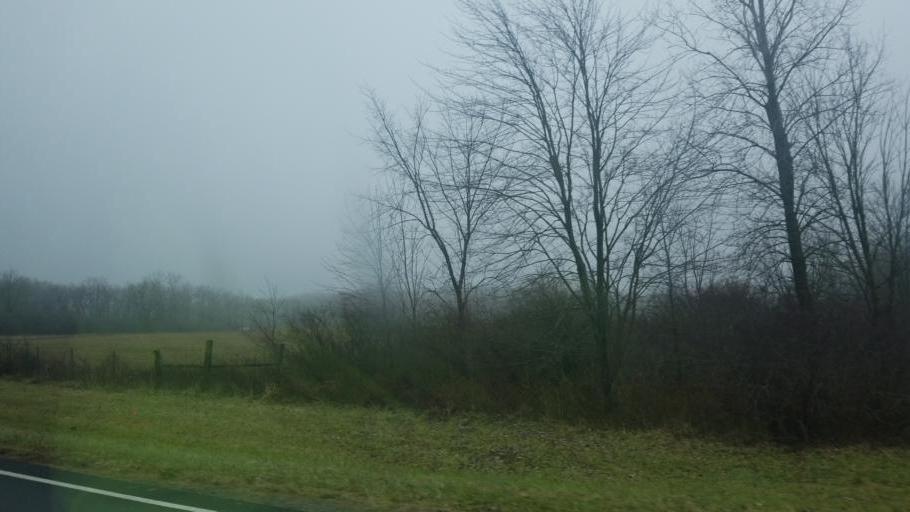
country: US
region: Ohio
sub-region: Champaign County
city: North Lewisburg
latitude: 40.2680
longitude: -83.4852
